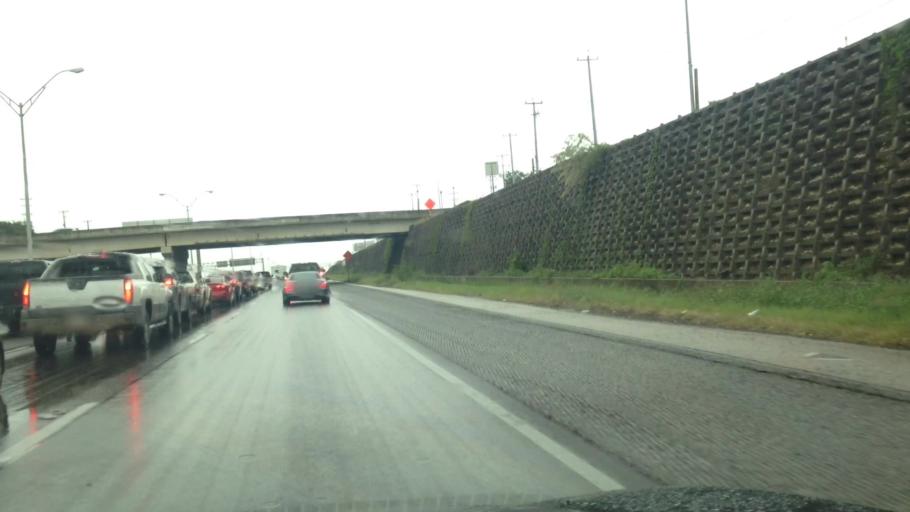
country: US
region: Texas
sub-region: Bexar County
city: Shavano Park
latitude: 29.5920
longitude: -98.5878
